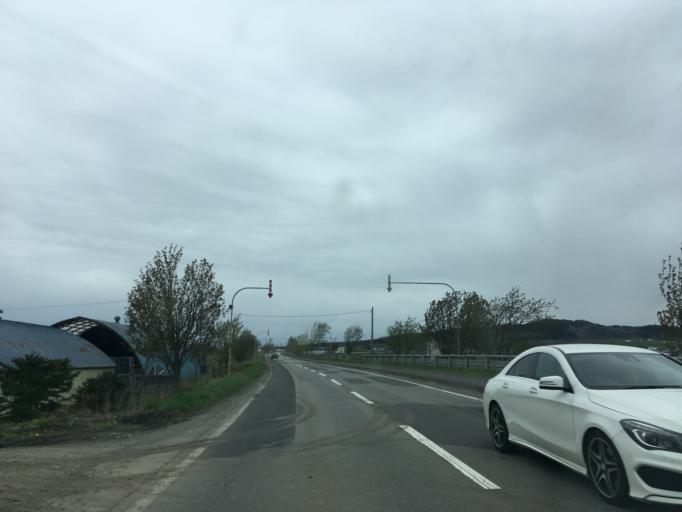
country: JP
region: Hokkaido
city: Chitose
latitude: 42.9492
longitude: 141.7884
